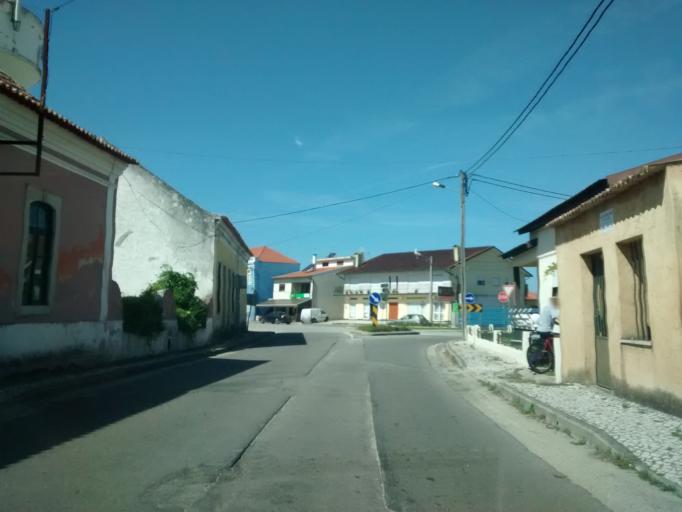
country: PT
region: Coimbra
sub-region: Mira
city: Mira
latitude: 40.4333
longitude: -8.7285
